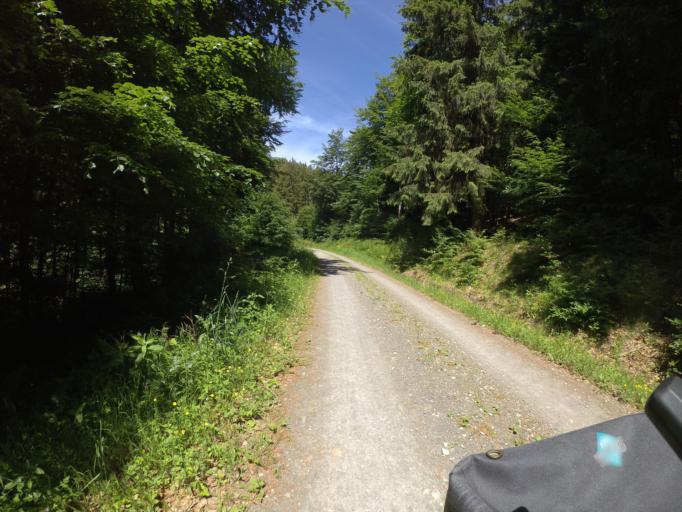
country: DE
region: Rheinland-Pfalz
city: Wirschweiler
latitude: 49.7610
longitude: 7.1178
